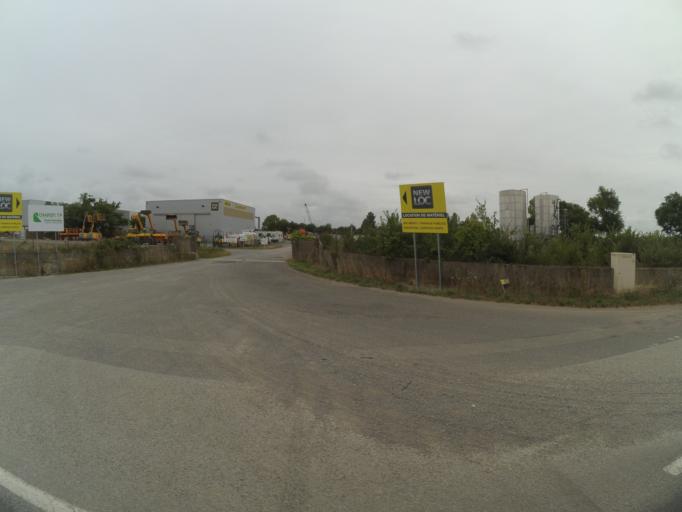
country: FR
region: Pays de la Loire
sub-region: Departement de la Vendee
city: Sallertaine
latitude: 46.8642
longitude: -1.9208
